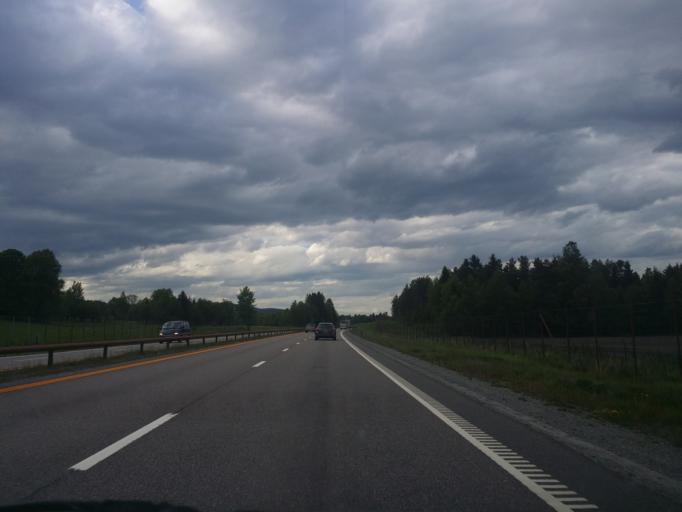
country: NO
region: Akershus
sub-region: Eidsvoll
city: Eidsvoll
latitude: 60.3627
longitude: 11.2043
